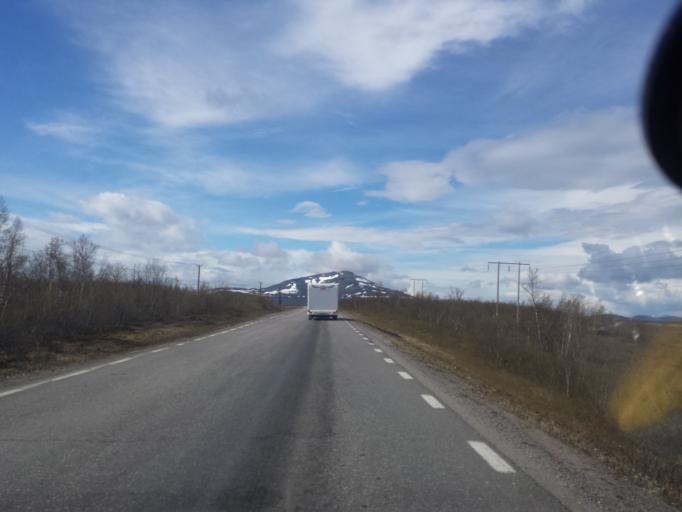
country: SE
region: Norrbotten
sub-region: Kiruna Kommun
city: Kiruna
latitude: 68.1137
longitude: 19.8309
